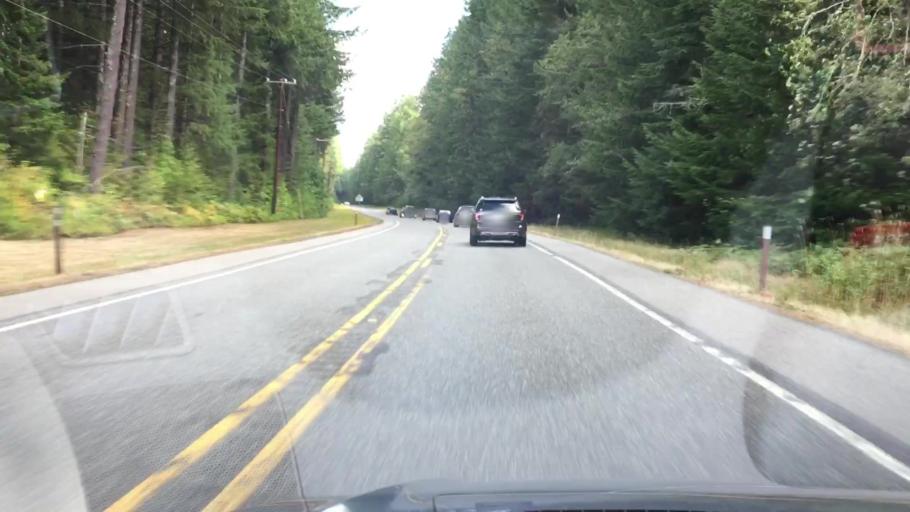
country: US
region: Washington
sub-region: Pierce County
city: Eatonville
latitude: 46.7534
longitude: -122.1088
